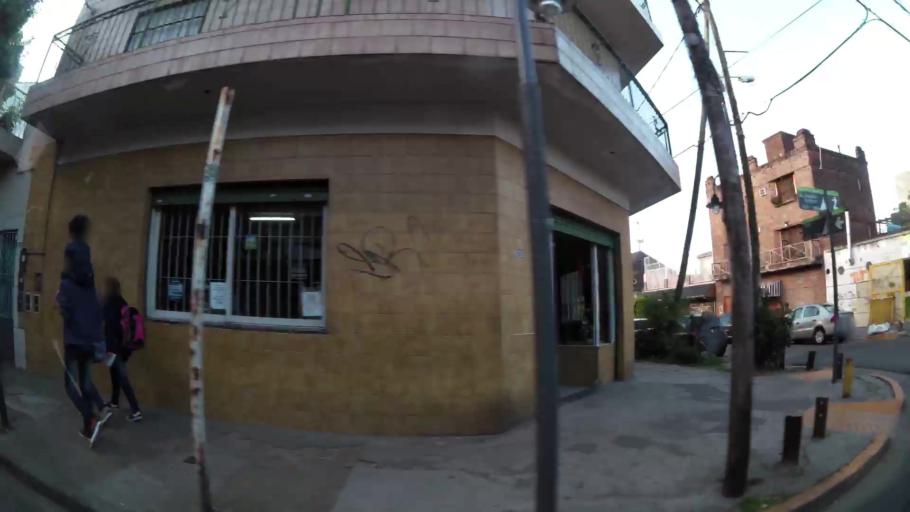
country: AR
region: Buenos Aires
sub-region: Partido de Tigre
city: Tigre
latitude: -34.4510
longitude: -58.5711
